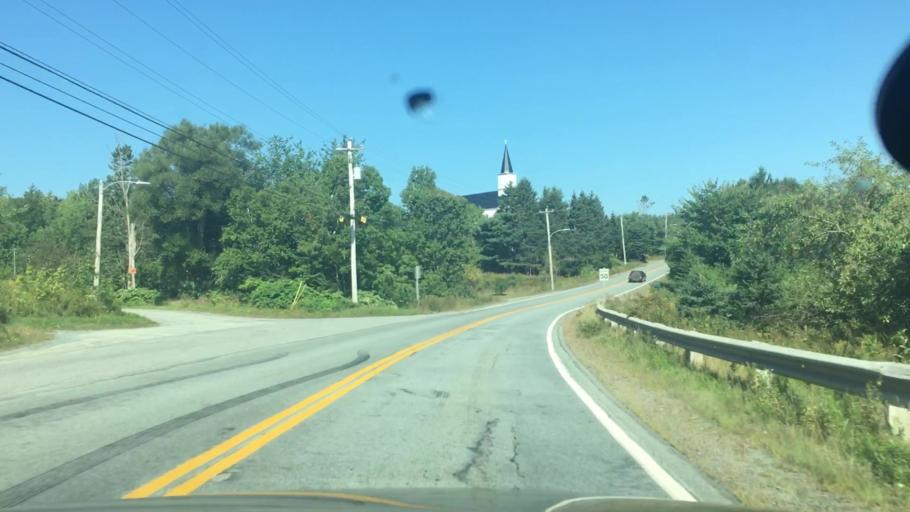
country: CA
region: Nova Scotia
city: New Glasgow
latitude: 44.9222
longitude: -62.5451
